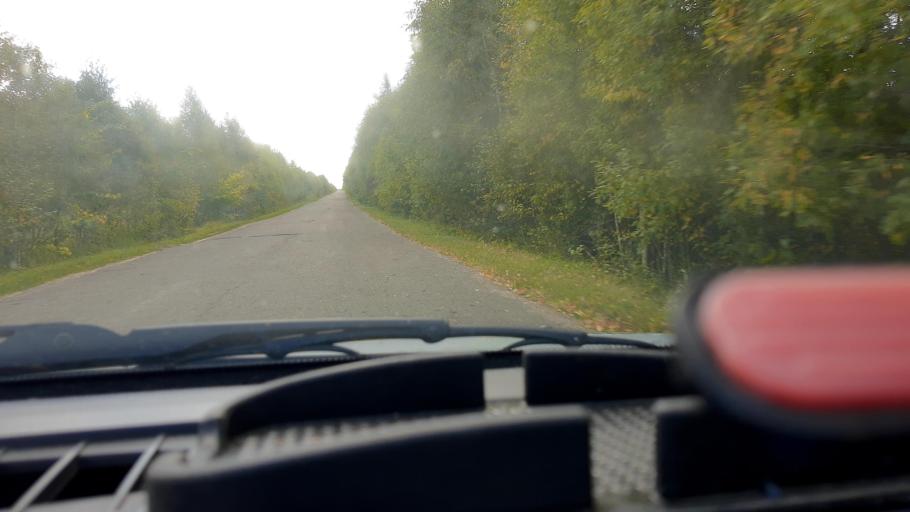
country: RU
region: Mariy-El
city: Kilemary
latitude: 56.9070
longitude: 46.7343
